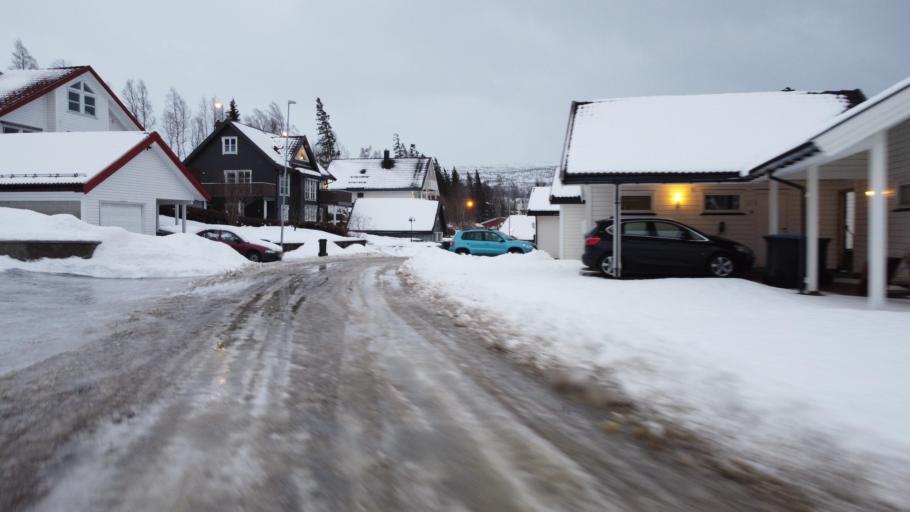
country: NO
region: Nordland
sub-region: Rana
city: Mo i Rana
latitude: 66.3308
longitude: 14.1544
